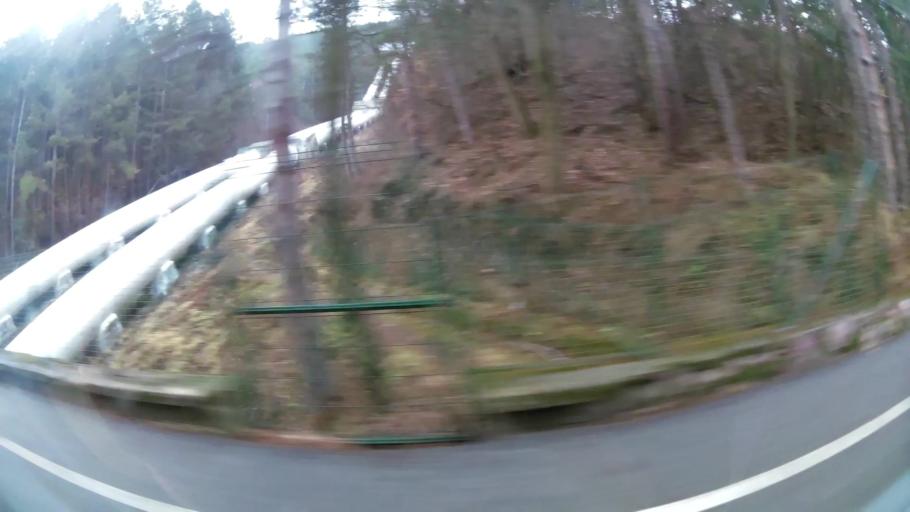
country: BG
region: Sofia-Capital
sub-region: Stolichna Obshtina
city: Sofia
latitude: 42.5838
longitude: 23.4285
